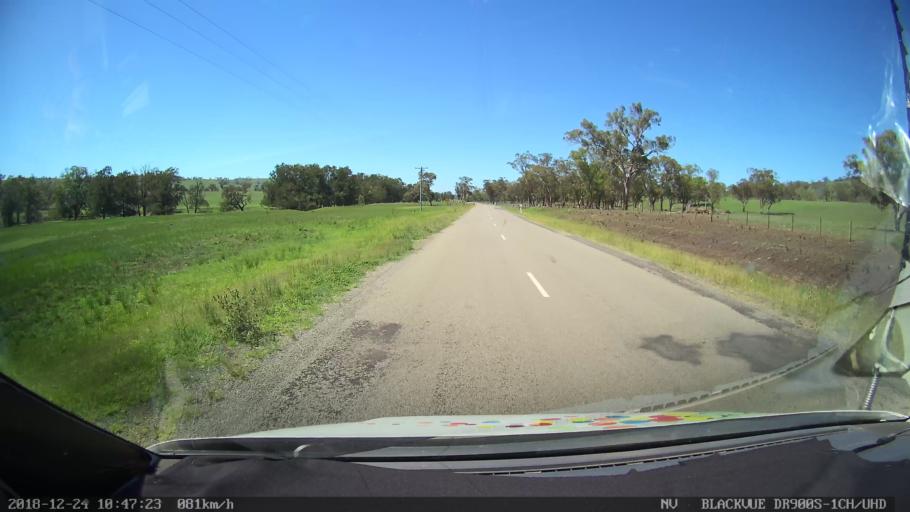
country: AU
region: New South Wales
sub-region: Upper Hunter Shire
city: Merriwa
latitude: -31.9239
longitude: 150.4296
